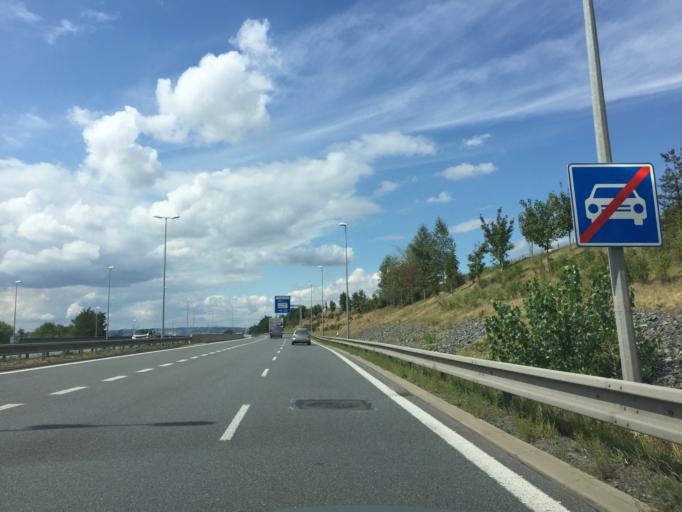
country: CZ
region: Praha
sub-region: Praha 9
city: Vysocany
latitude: 50.1156
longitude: 14.5314
